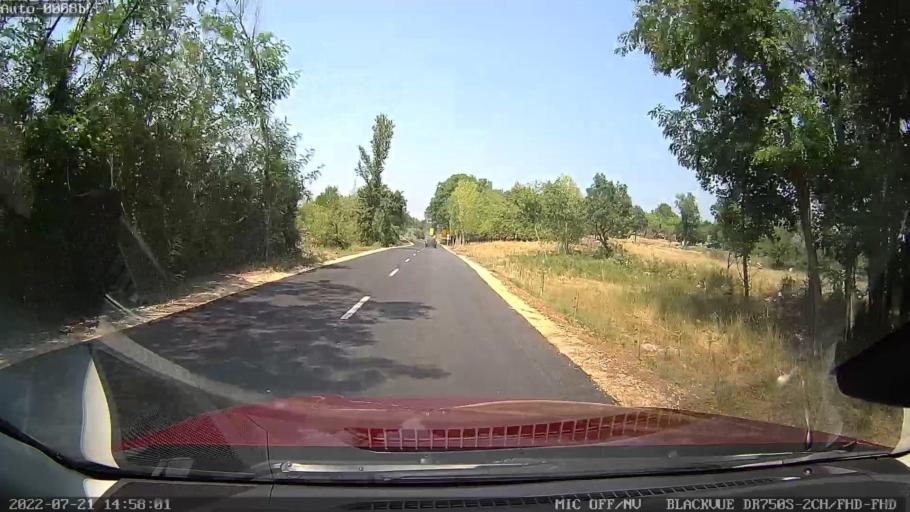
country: HR
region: Istarska
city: Pazin
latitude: 45.2130
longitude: 13.9554
